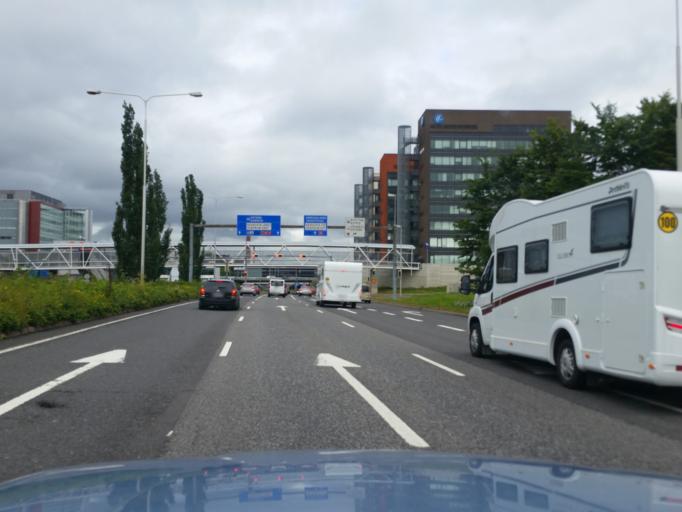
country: FI
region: Varsinais-Suomi
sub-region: Turku
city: Turku
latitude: 60.4486
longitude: 22.3006
